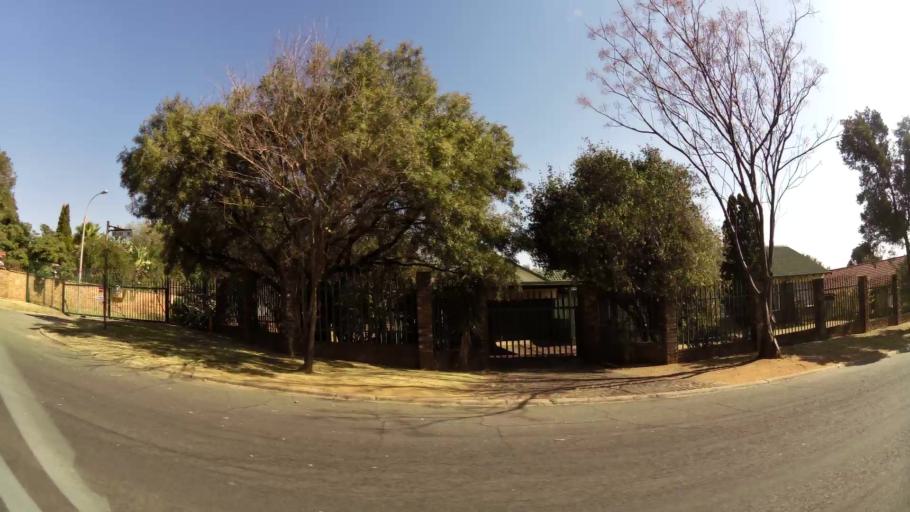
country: ZA
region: Gauteng
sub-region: Ekurhuleni Metropolitan Municipality
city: Tembisa
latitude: -26.0432
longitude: 28.2305
